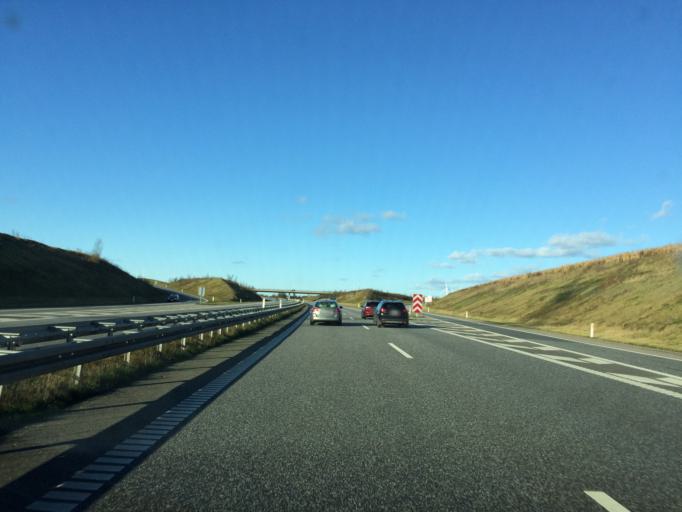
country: DK
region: South Denmark
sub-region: Vejle Kommune
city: Vejle
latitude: 55.7992
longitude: 9.5654
